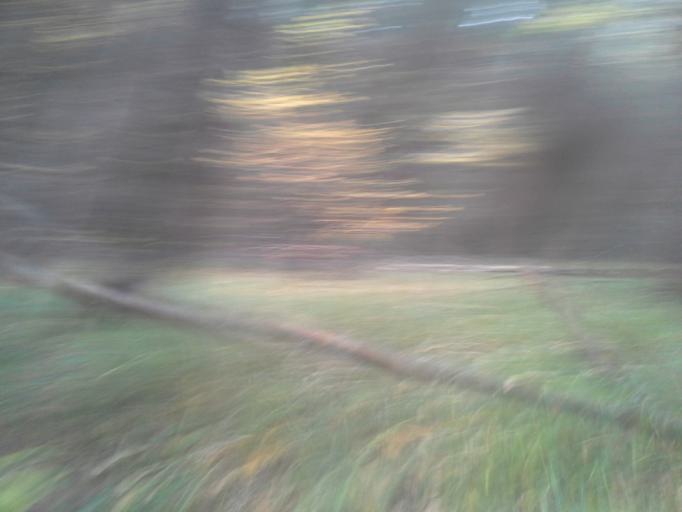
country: RU
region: Moskovskaya
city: Selyatino
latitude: 55.4676
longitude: 36.9721
